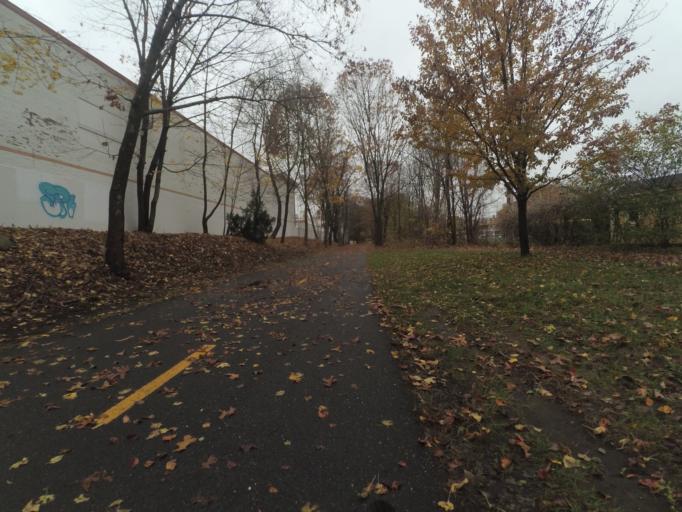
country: US
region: Massachusetts
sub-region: Middlesex County
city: Belmont
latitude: 42.4255
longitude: -71.1872
